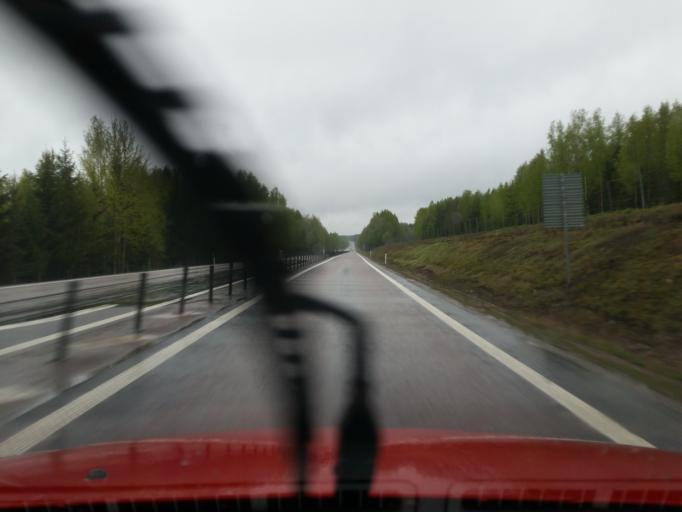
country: SE
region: Dalarna
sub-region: Saters Kommun
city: Saeter
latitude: 60.3763
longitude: 15.6896
